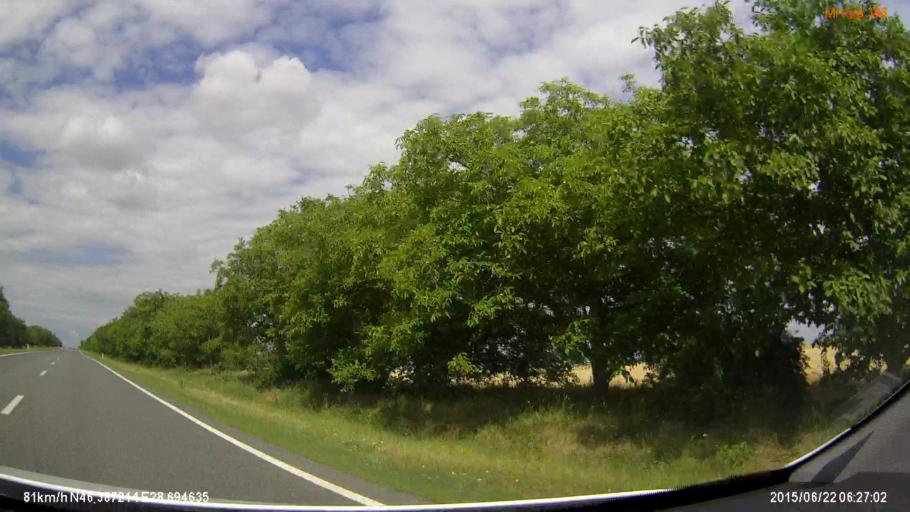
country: MD
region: Gagauzia
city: Bugeac
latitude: 46.3869
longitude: 28.6943
